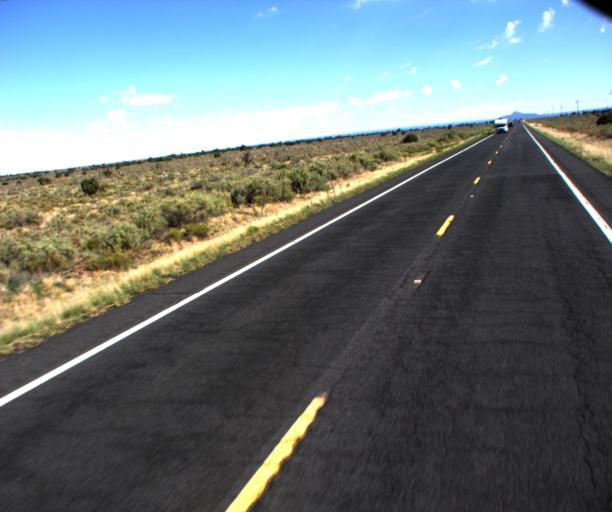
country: US
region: Arizona
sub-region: Coconino County
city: Williams
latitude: 35.5932
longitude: -112.1491
